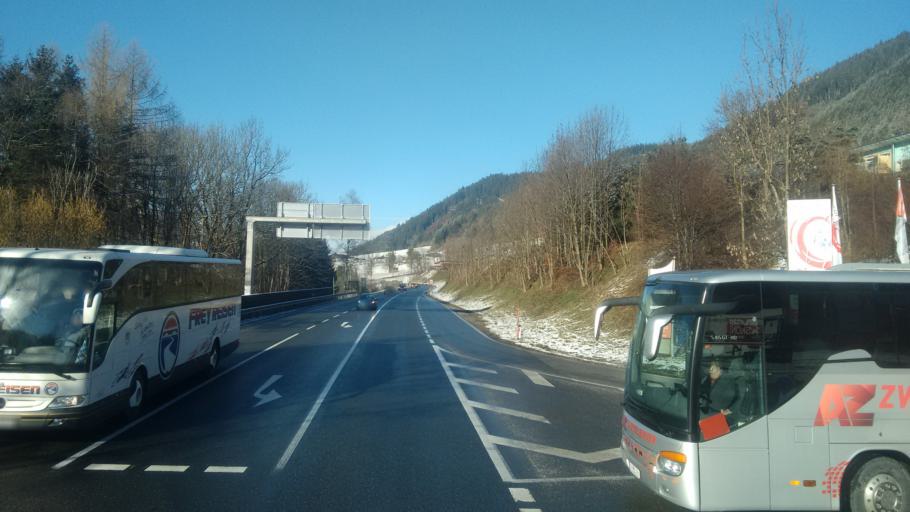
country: AT
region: Styria
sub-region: Politischer Bezirk Liezen
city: Schladming
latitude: 47.3966
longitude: 13.6832
